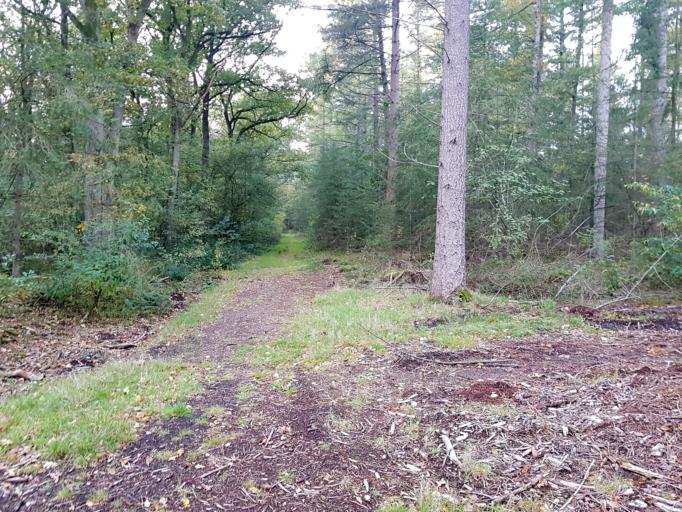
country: NL
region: Utrecht
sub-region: Gemeente Utrechtse Heuvelrug
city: Maarsbergen
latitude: 52.0363
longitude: 5.4070
